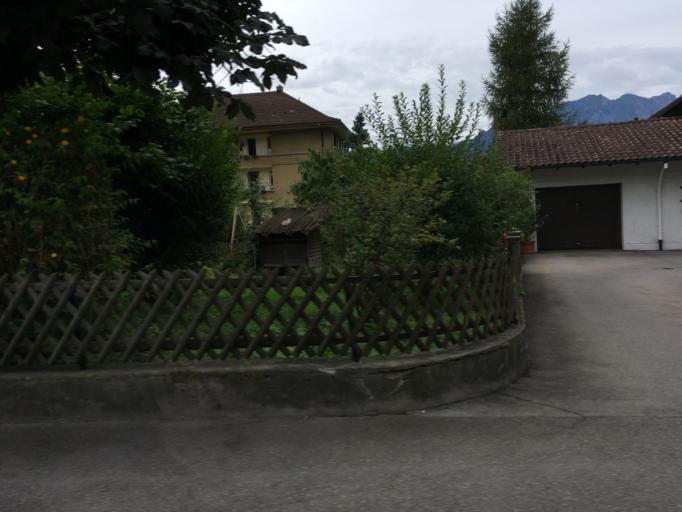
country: CH
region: Bern
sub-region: Thun District
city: Thun
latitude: 46.7465
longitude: 7.6419
